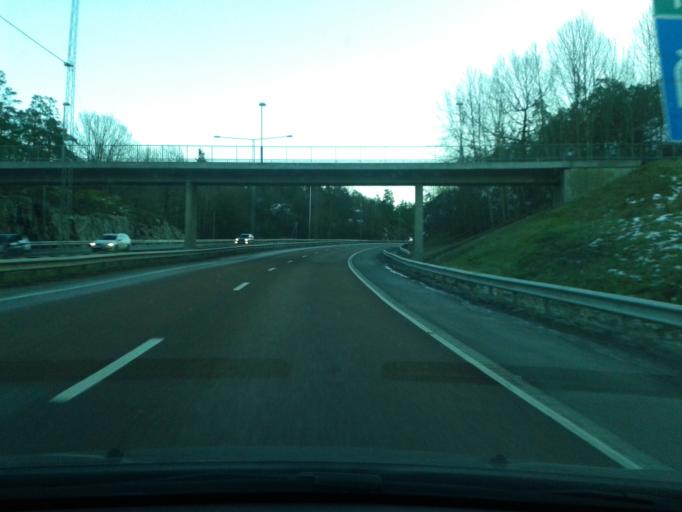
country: SE
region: Stockholm
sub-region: Nacka Kommun
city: Alta
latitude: 59.2566
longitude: 18.1683
